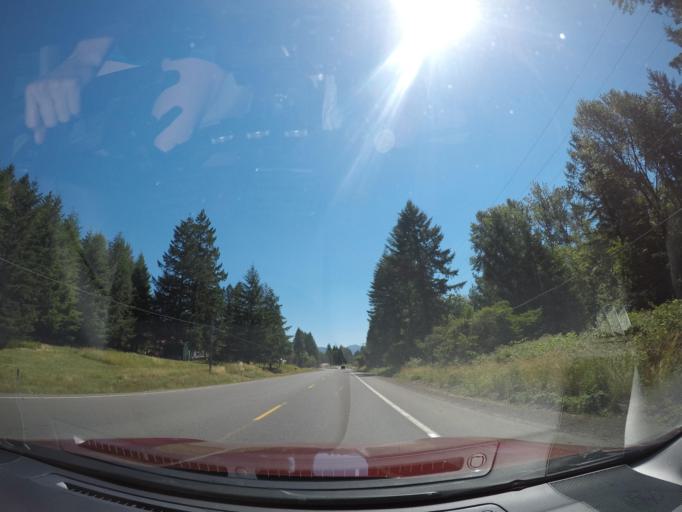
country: US
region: Oregon
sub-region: Linn County
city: Mill City
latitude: 44.7569
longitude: -122.4421
